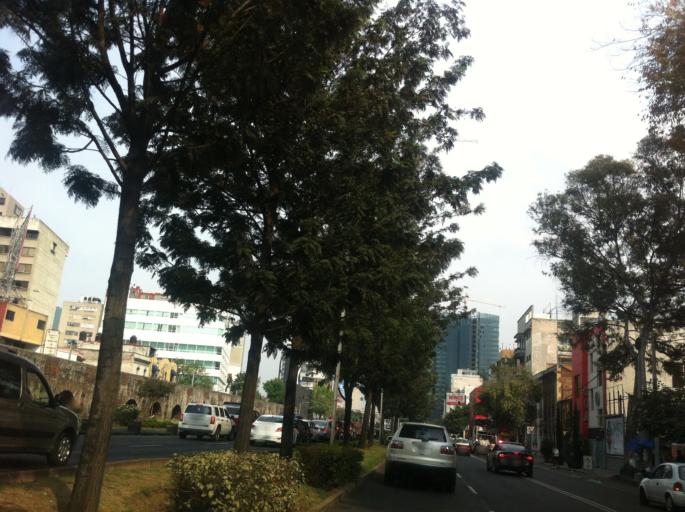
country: MX
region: Mexico City
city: Benito Juarez
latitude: 19.4222
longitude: -99.1685
